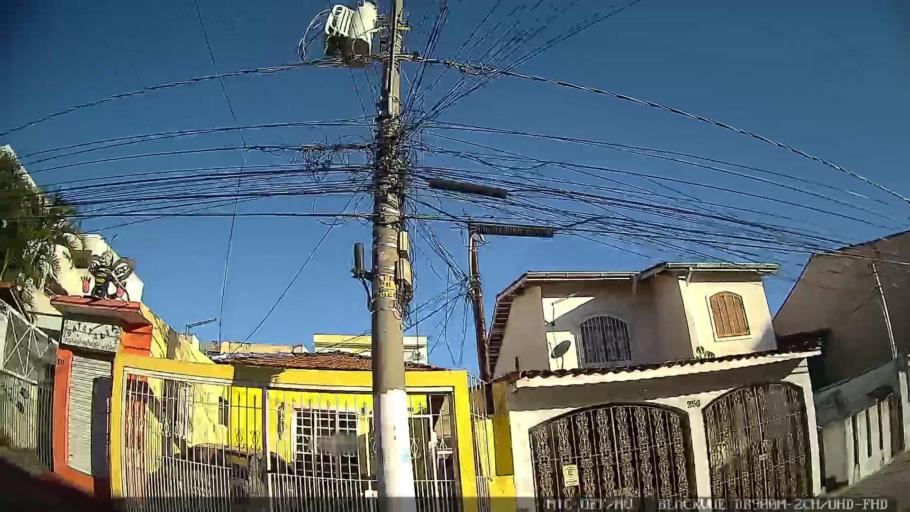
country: BR
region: Sao Paulo
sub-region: Guarulhos
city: Guarulhos
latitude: -23.5379
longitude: -46.5131
